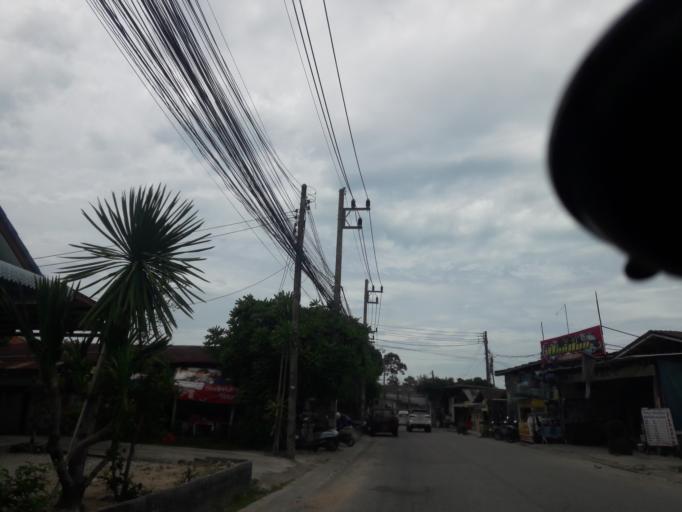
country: TH
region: Surat Thani
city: Ko Samui
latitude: 9.5350
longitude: 100.0439
